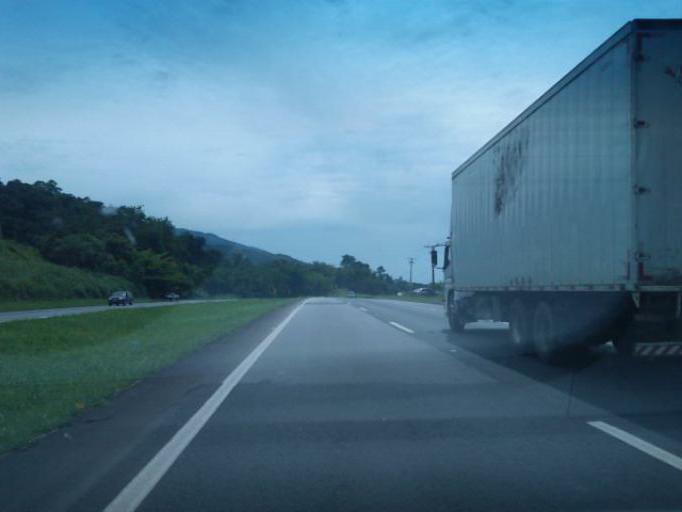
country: BR
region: Sao Paulo
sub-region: Miracatu
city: Miracatu
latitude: -24.2790
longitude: -47.4219
